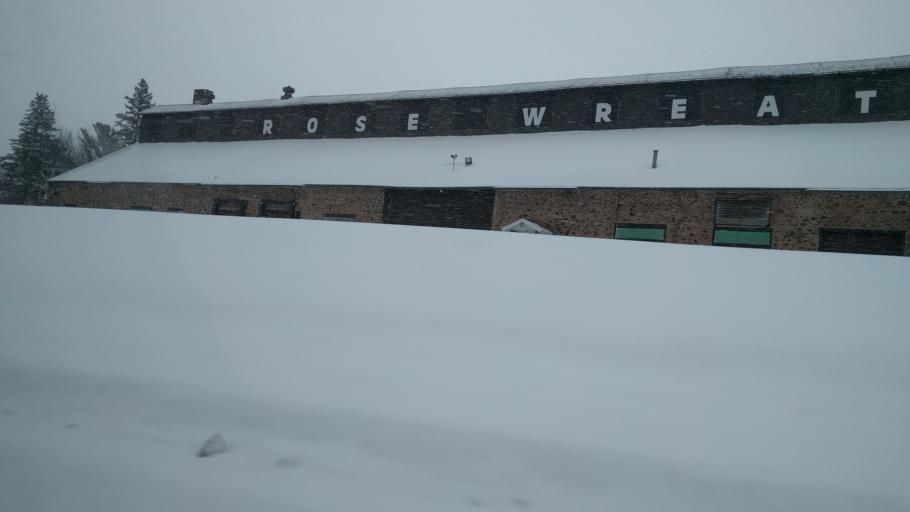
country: US
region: Wisconsin
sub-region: Iron County
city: Hurley
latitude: 46.4286
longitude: -90.2383
